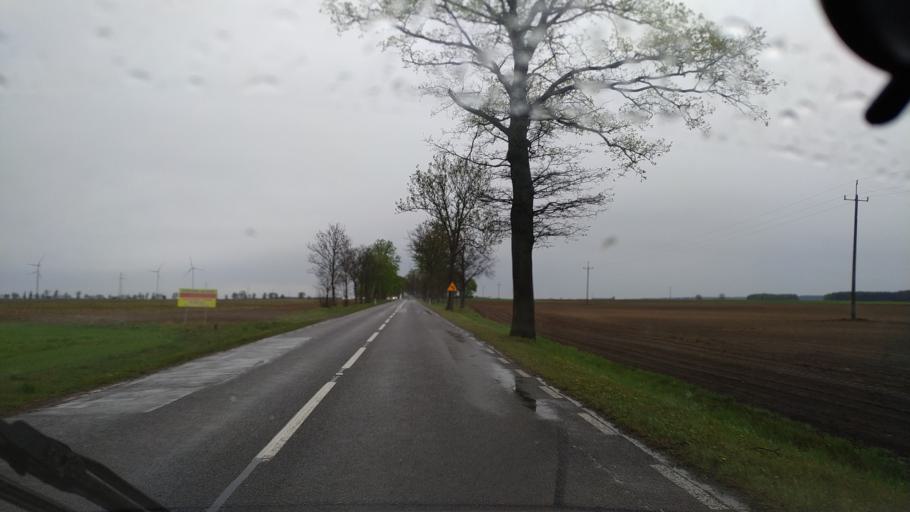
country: PL
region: Greater Poland Voivodeship
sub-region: Powiat zlotowski
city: Krajenka
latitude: 53.3196
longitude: 16.9961
